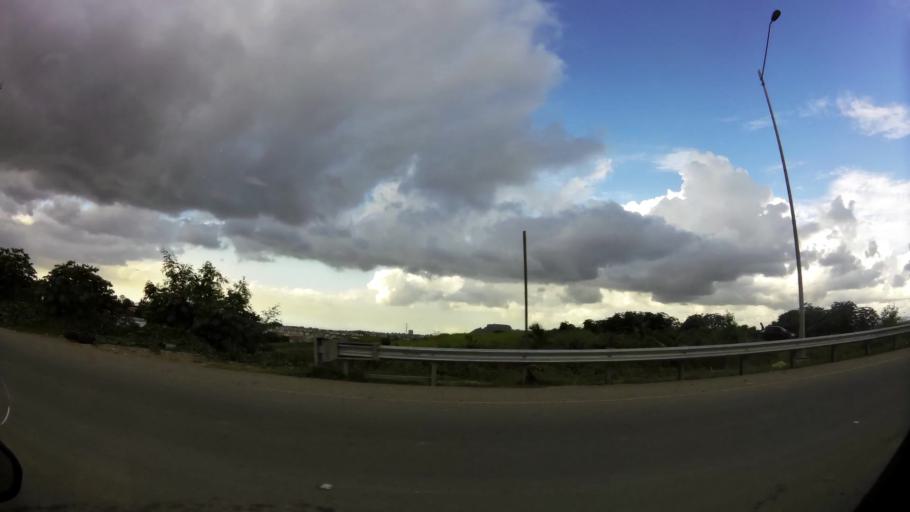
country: TT
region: City of San Fernando
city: Mon Repos
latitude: 10.2446
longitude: -61.4452
